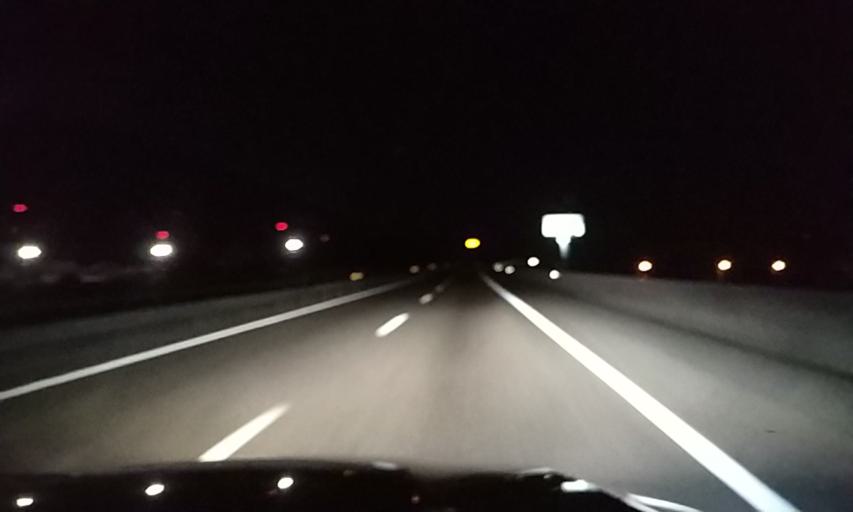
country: PT
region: Santarem
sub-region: Alcanena
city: Alcanena
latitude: 39.5371
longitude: -8.6609
